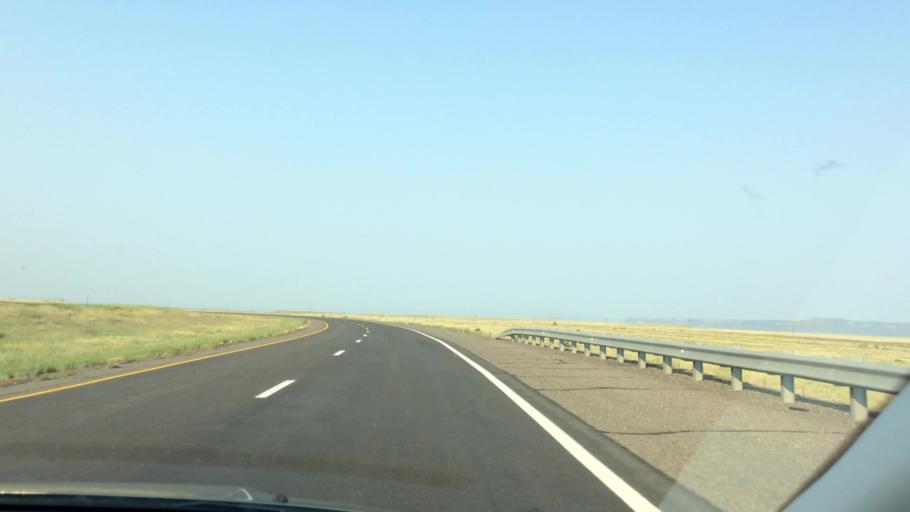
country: US
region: New Mexico
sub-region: Colfax County
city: Raton
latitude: 36.7219
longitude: -104.4707
